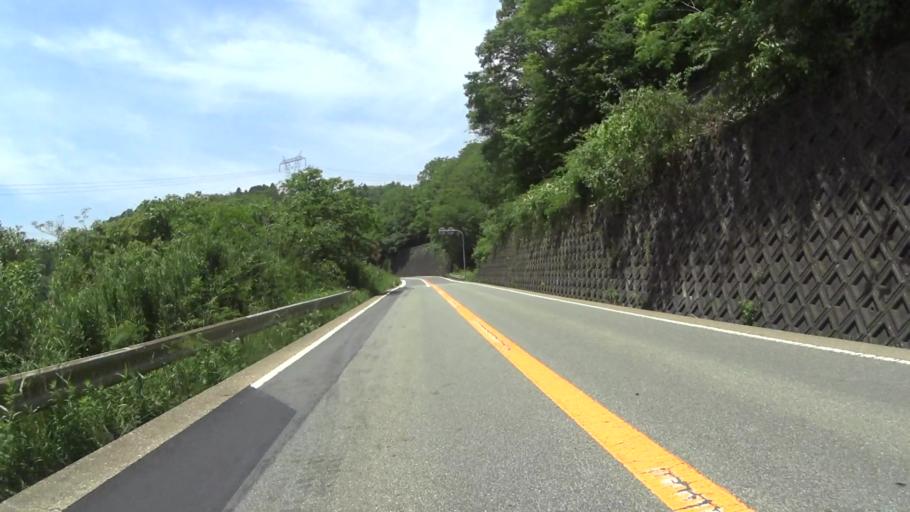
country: JP
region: Kyoto
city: Ayabe
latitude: 35.1889
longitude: 135.3355
